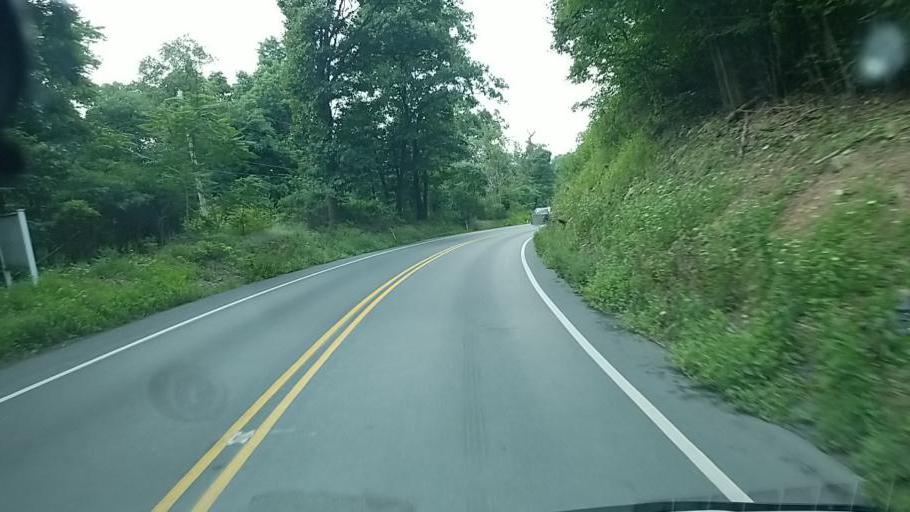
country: US
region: Pennsylvania
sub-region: Dauphin County
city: Elizabethville
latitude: 40.5343
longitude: -76.8191
